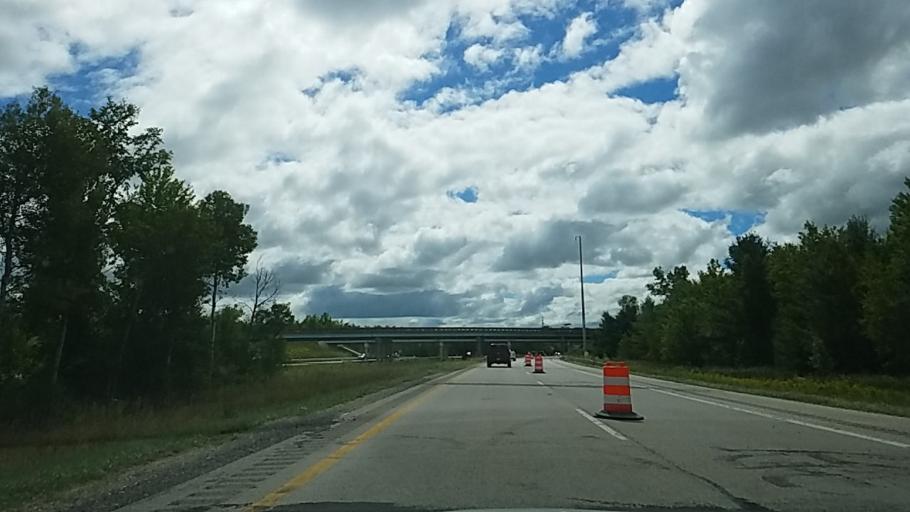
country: US
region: Michigan
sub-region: Arenac County
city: Standish
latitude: 43.9505
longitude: -84.0147
